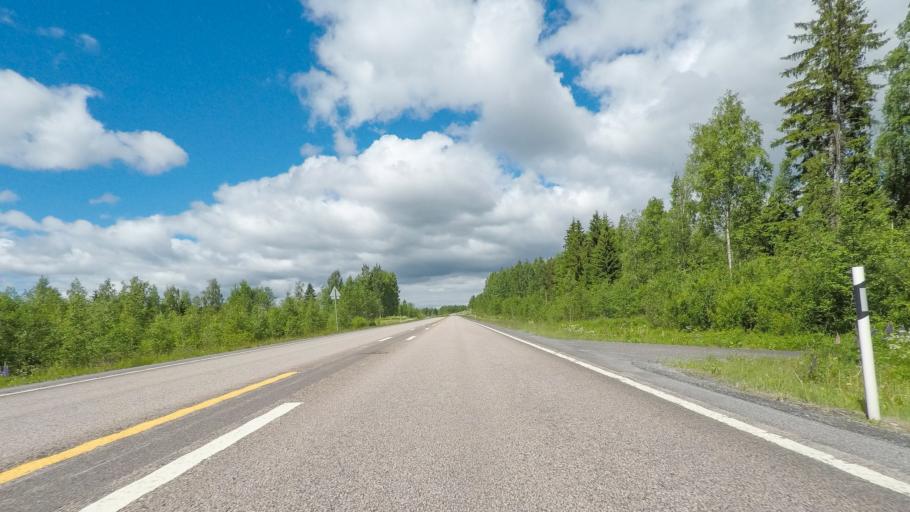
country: FI
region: Paijanne Tavastia
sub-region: Lahti
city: Hartola
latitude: 61.4079
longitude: 26.0431
